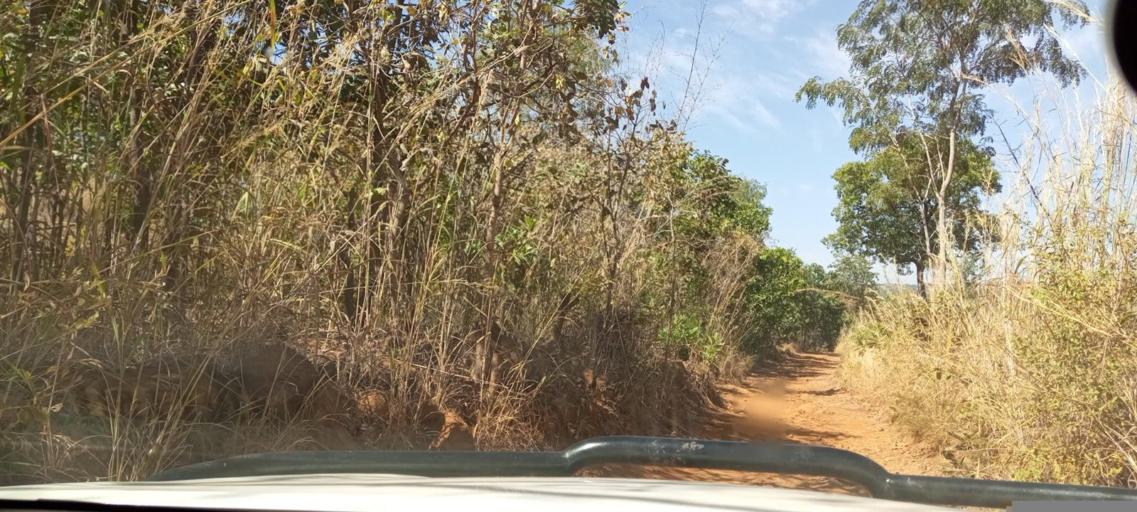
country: ML
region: Koulikoro
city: Kangaba
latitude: 12.3263
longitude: -8.6706
